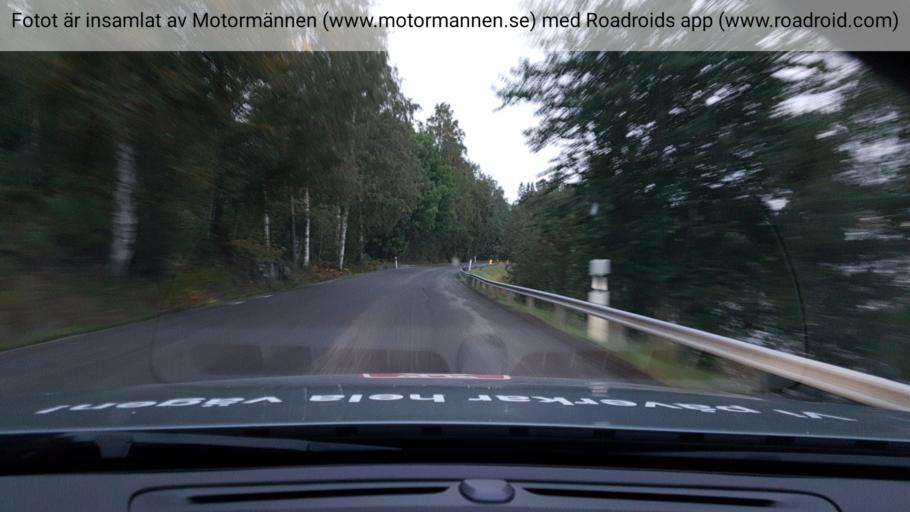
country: SE
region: OErebro
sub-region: Nora Kommun
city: As
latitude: 59.4909
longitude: 14.9412
